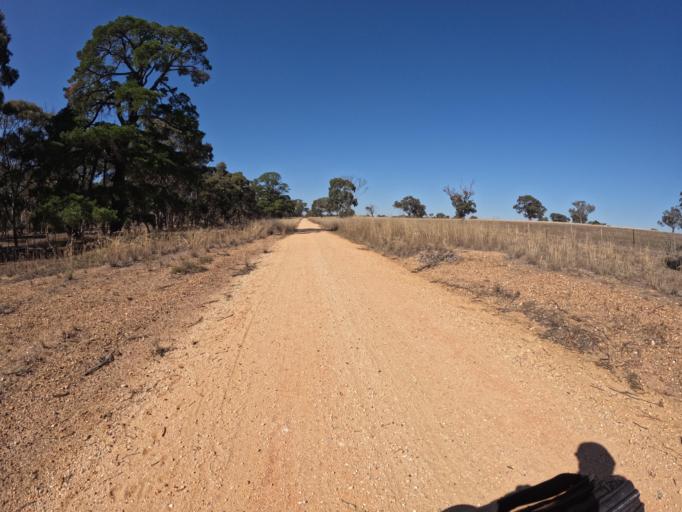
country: AU
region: Victoria
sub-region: Greater Bendigo
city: Kennington
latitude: -36.8356
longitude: 144.5969
